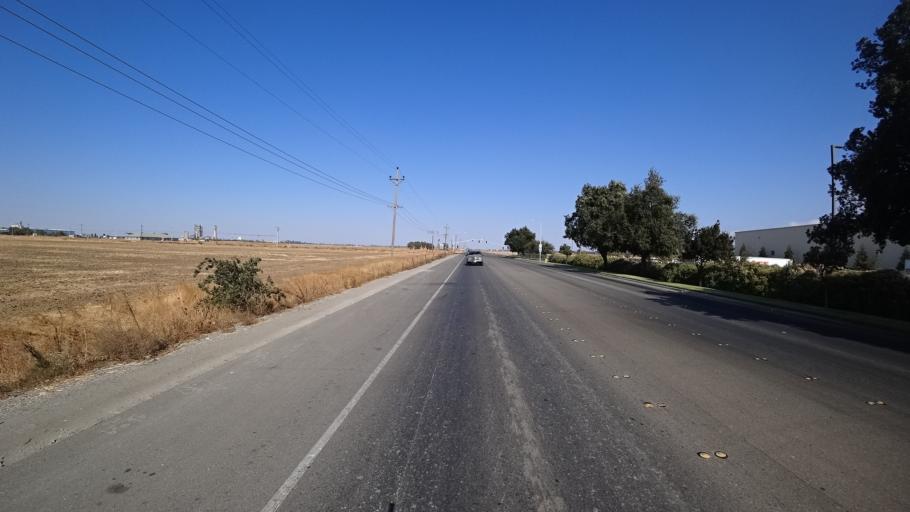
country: US
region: California
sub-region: Yolo County
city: Woodland
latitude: 38.6829
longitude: -121.7285
